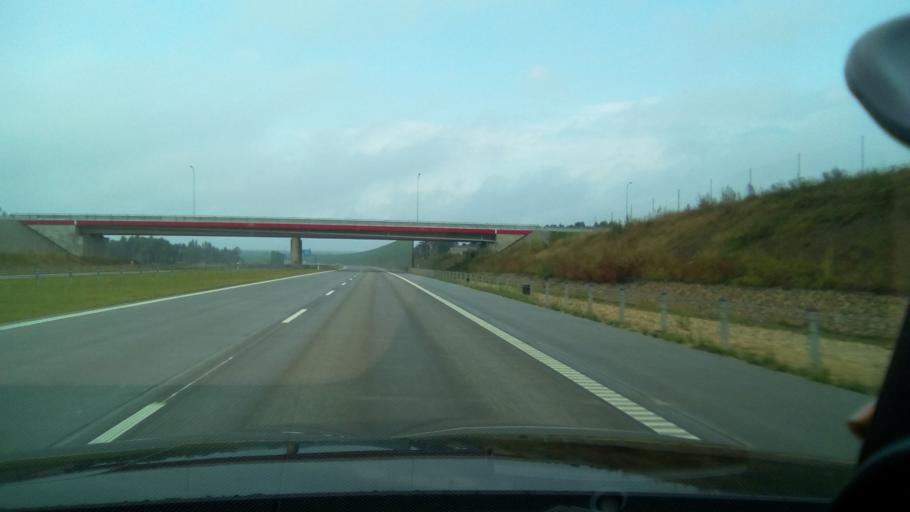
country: PL
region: Silesian Voivodeship
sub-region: Powiat klobucki
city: Kalej
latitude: 50.8020
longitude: 19.0081
